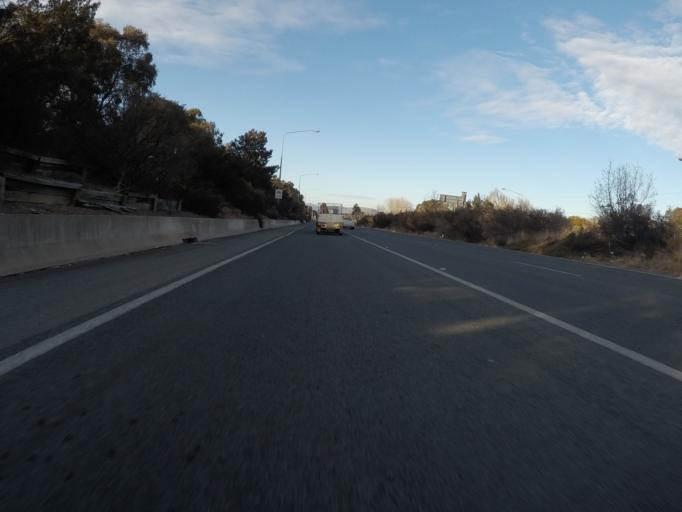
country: AU
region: Australian Capital Territory
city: Forrest
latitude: -35.3335
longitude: 149.1619
